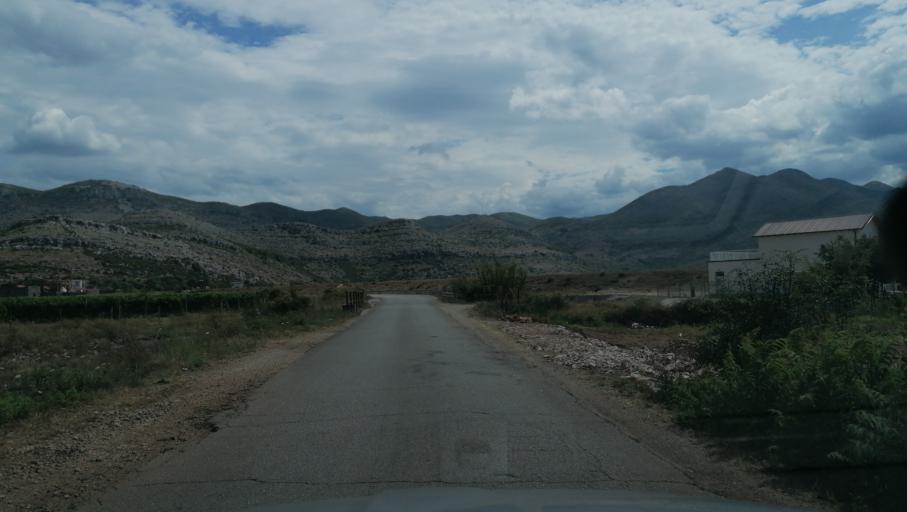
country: BA
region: Republika Srpska
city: Trebinje
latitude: 42.6680
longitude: 18.3240
